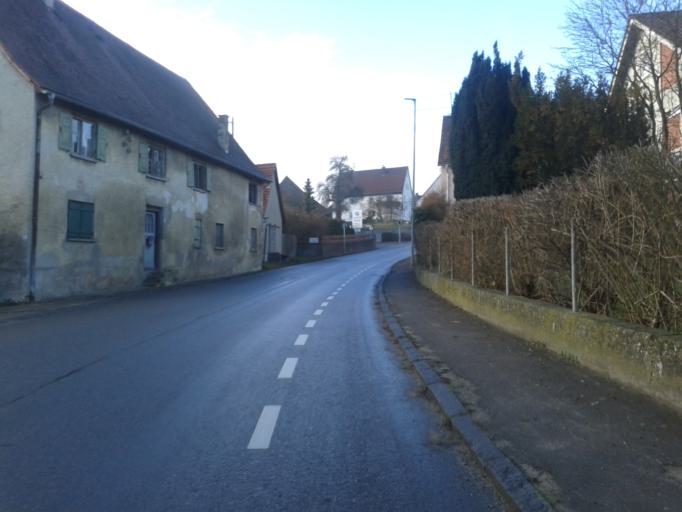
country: DE
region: Baden-Wuerttemberg
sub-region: Tuebingen Region
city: Erbach
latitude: 48.3813
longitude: 9.8989
